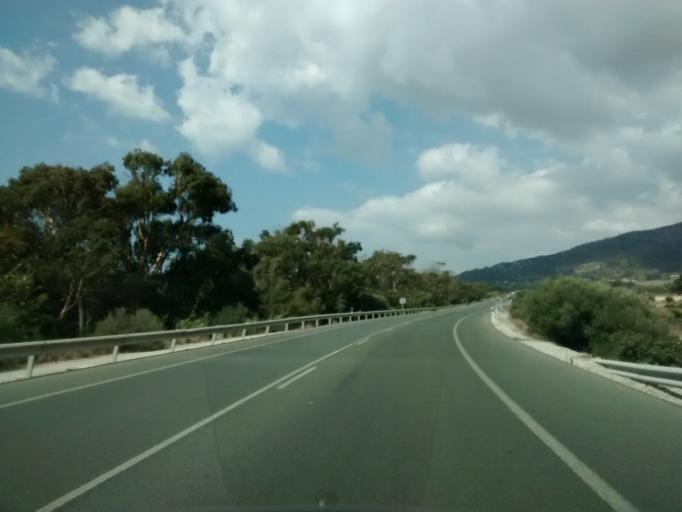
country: ES
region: Andalusia
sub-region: Provincia de Cadiz
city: Tarifa
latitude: 36.0450
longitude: -5.6338
